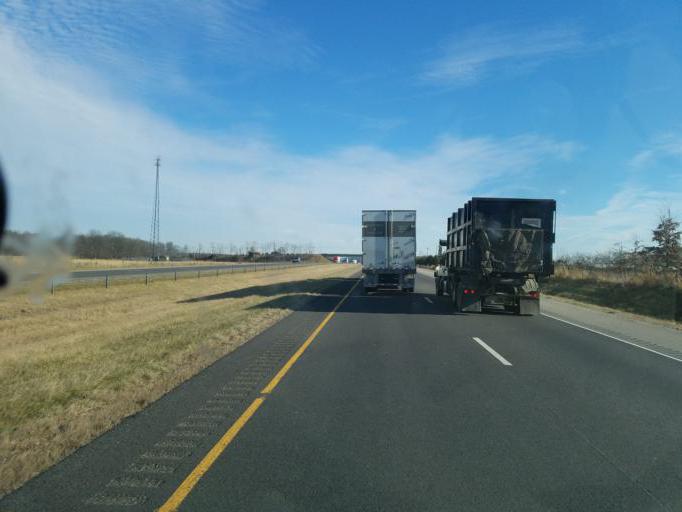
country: US
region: Indiana
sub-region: Wayne County
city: Centerville
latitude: 39.8574
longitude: -85.0472
